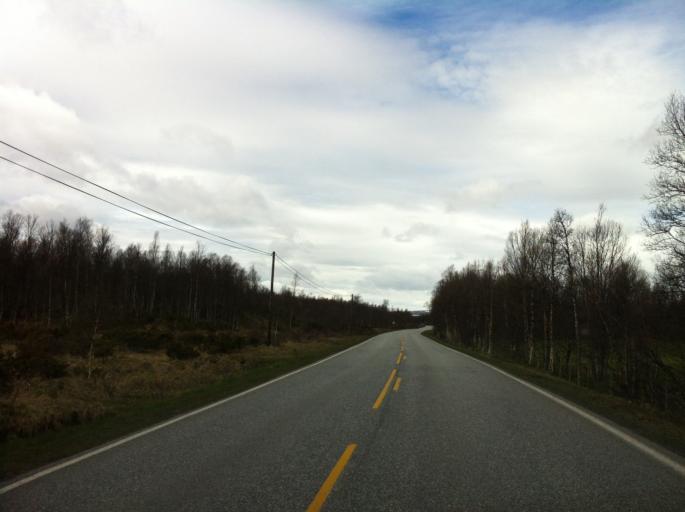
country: NO
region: Sor-Trondelag
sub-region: Roros
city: Roros
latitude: 62.5969
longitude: 11.7000
